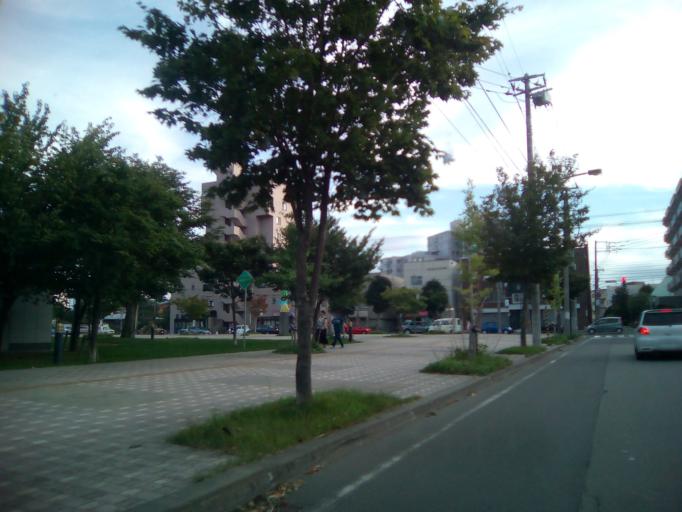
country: JP
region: Hokkaido
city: Sapporo
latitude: 43.0438
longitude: 141.3748
